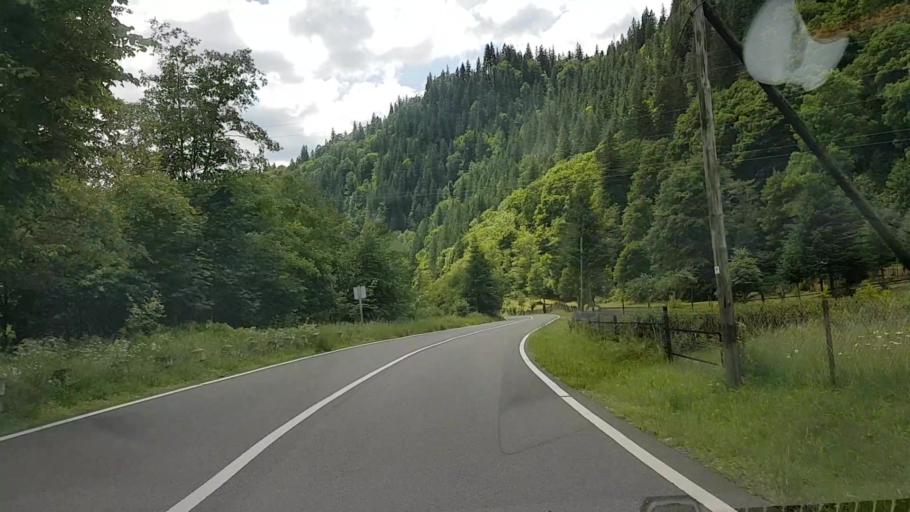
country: RO
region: Suceava
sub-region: Comuna Crucea
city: Crucea
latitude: 47.3195
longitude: 25.6272
